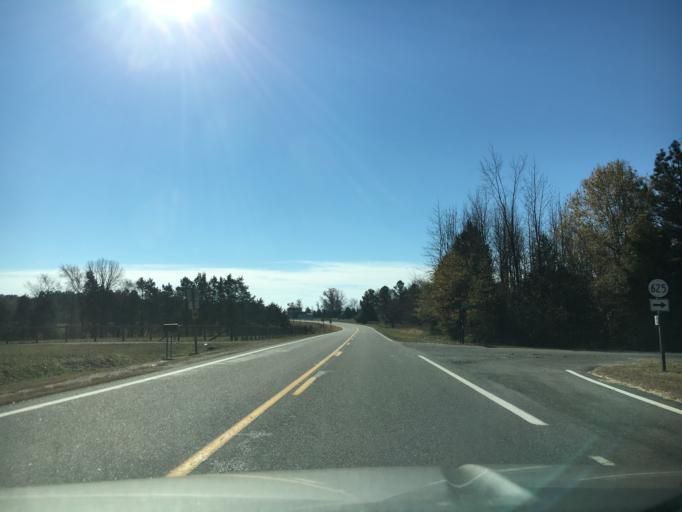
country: US
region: Virginia
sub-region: Cumberland County
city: Cumberland
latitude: 37.5866
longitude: -78.1745
